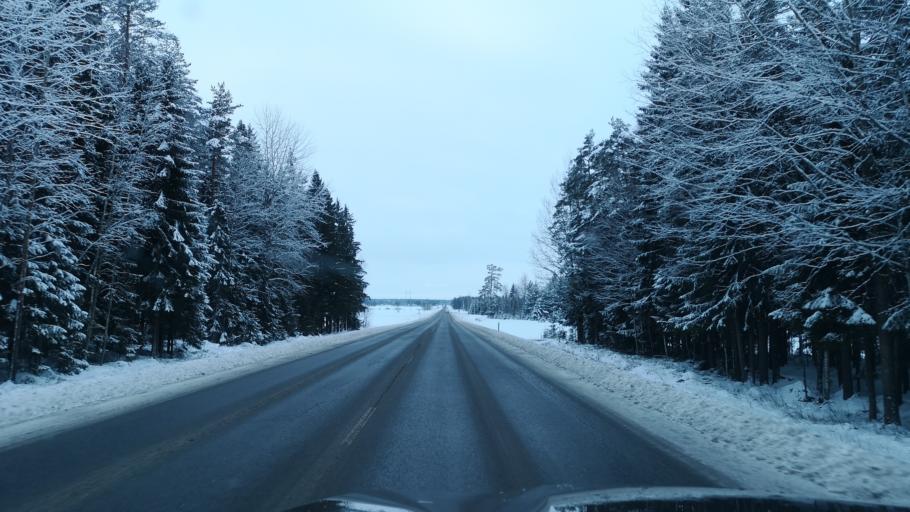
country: FI
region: Varsinais-Suomi
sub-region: Loimaa
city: Loimaa
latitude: 60.8987
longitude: 23.1313
